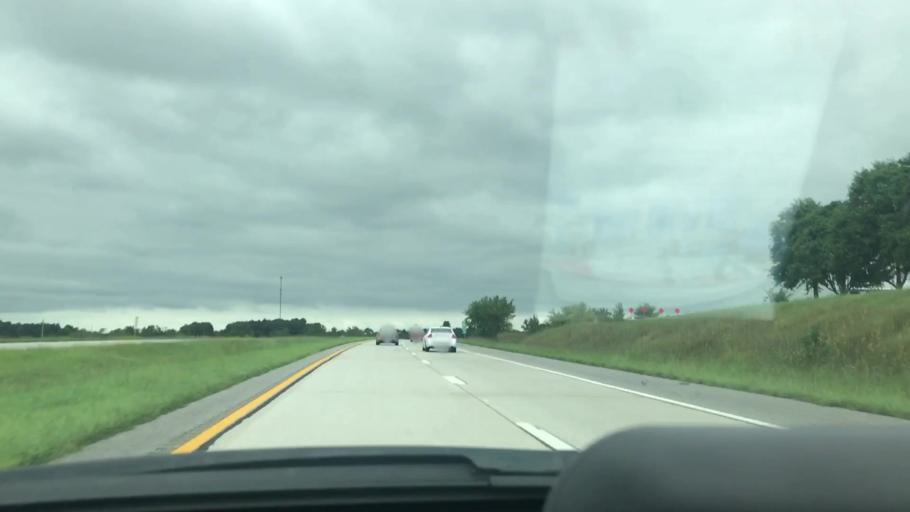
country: US
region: Missouri
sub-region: Greene County
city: Fair Grove
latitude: 37.4449
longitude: -93.1440
